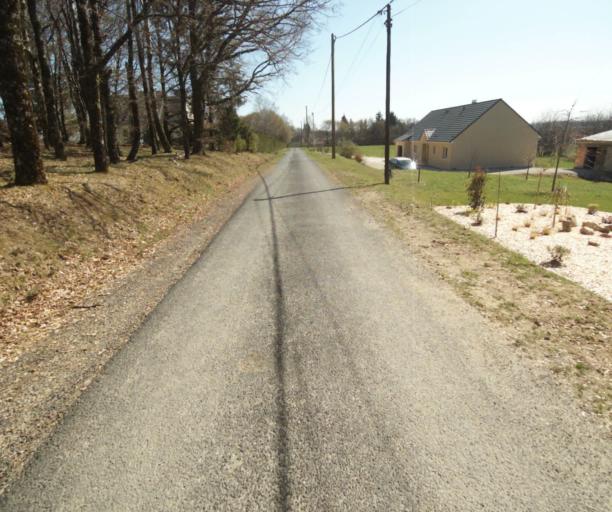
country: FR
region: Limousin
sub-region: Departement de la Correze
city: Saint-Clement
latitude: 45.3134
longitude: 1.6771
